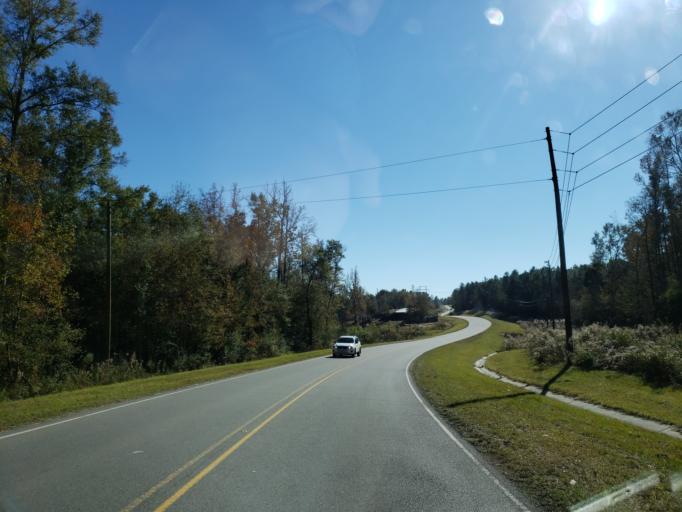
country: US
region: Mississippi
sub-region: Lamar County
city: Arnold Line
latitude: 31.3365
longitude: -89.3984
